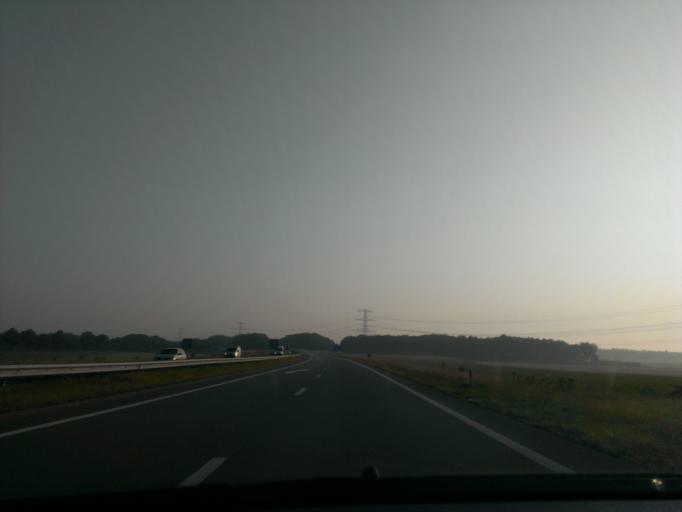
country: NL
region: Drenthe
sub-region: Gemeente Coevorden
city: Sleen
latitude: 52.7569
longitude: 6.8367
